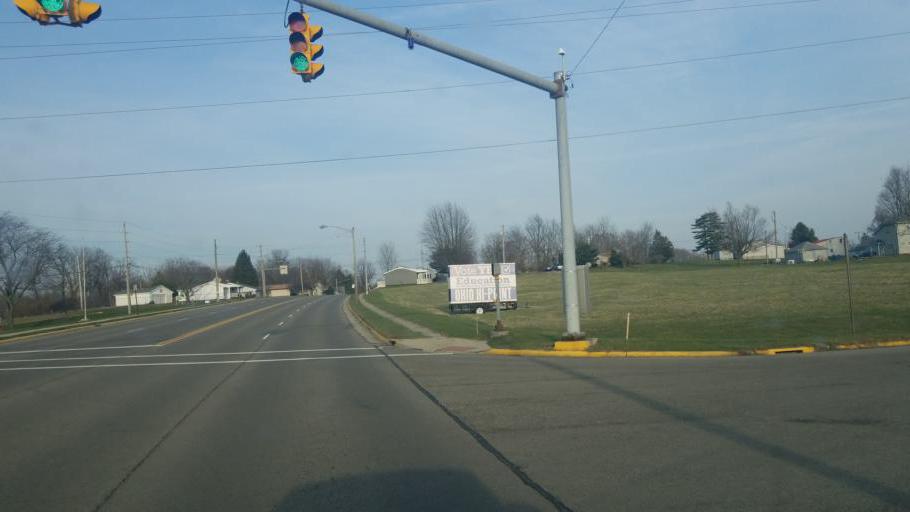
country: US
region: Ohio
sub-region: Logan County
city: Bellefontaine
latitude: 40.3635
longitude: -83.7789
